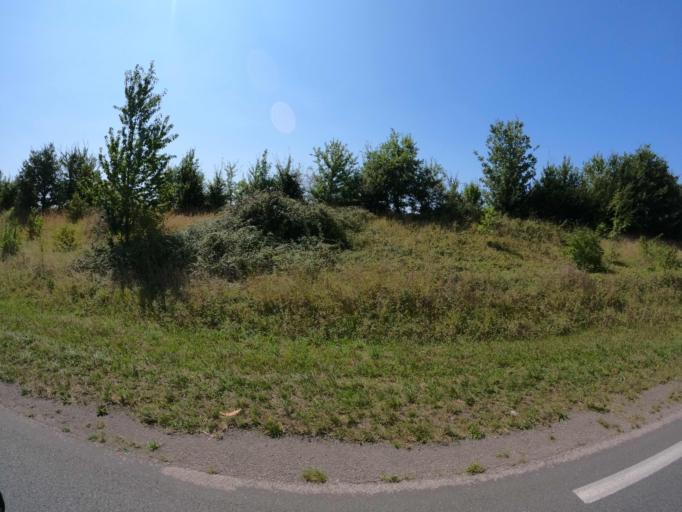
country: FR
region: Poitou-Charentes
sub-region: Departement des Deux-Sevres
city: Mougon
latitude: 46.2870
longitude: -0.2858
